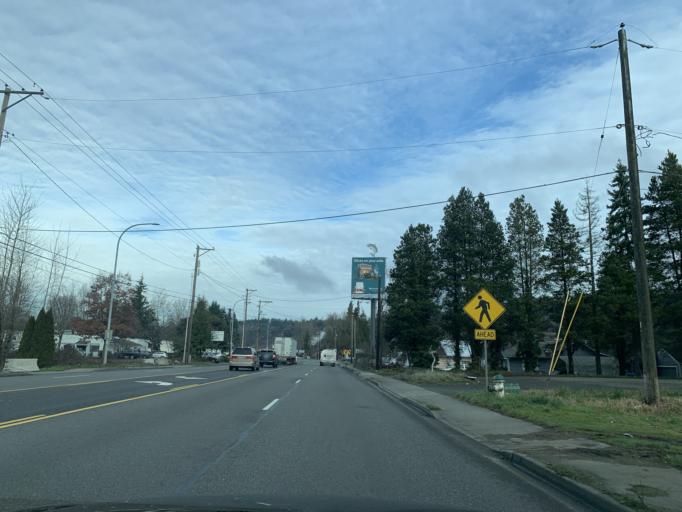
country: US
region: Washington
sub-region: Pierce County
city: Fife Heights
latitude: 47.2524
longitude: -122.3567
